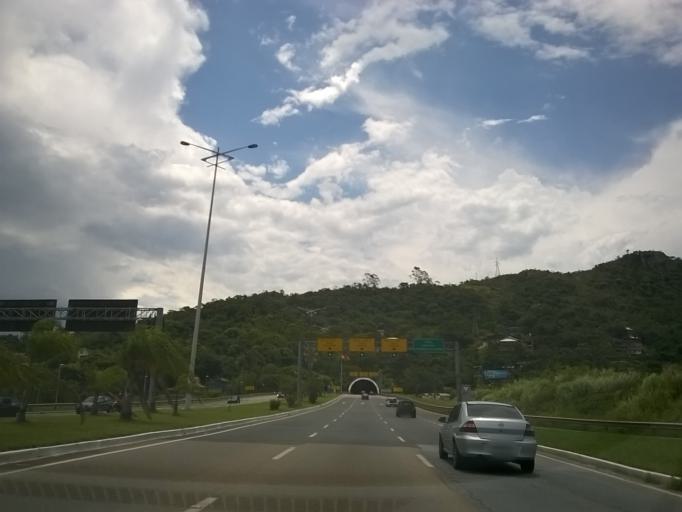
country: BR
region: Santa Catarina
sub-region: Florianopolis
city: Saco dos Limoes
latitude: -27.6110
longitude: -48.5371
